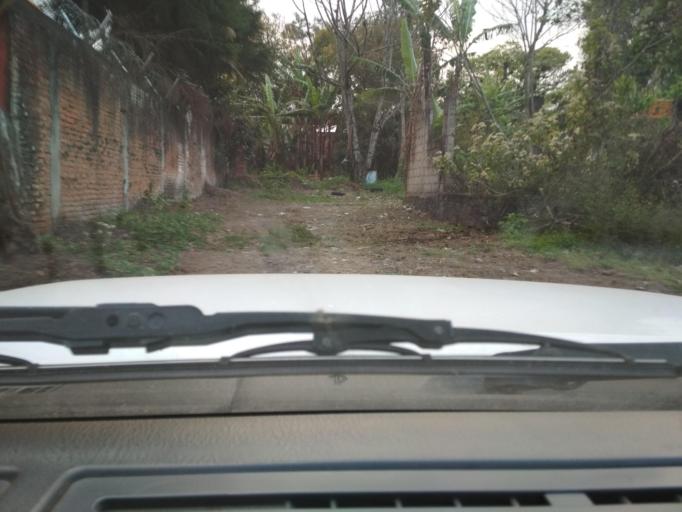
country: MX
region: Veracruz
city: Orizaba
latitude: 18.8613
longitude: -97.0924
